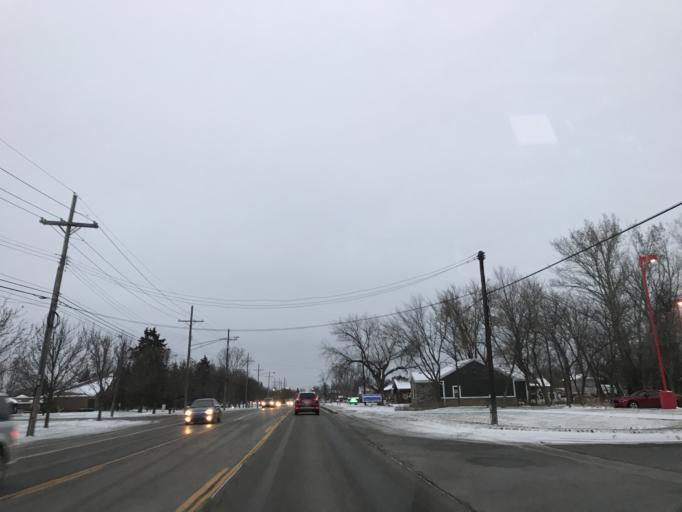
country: US
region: Michigan
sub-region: Oakland County
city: South Lyon
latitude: 42.4527
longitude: -83.6508
